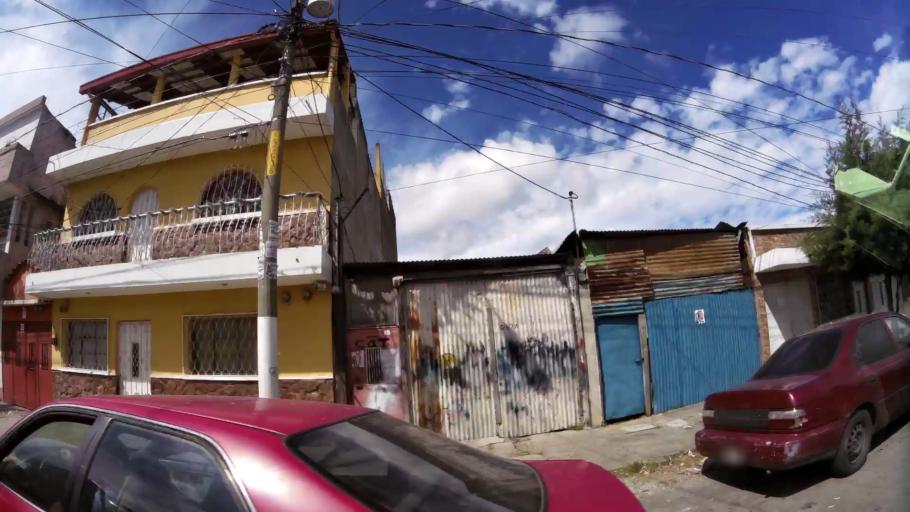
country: GT
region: Guatemala
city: Mixco
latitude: 14.6577
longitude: -90.5763
